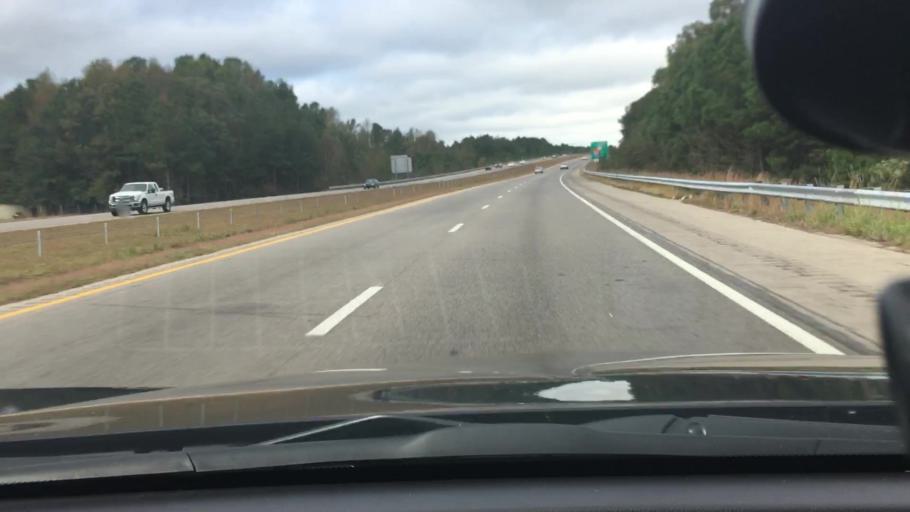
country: US
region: North Carolina
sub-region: Wilson County
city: Lucama
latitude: 35.7443
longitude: -78.0200
